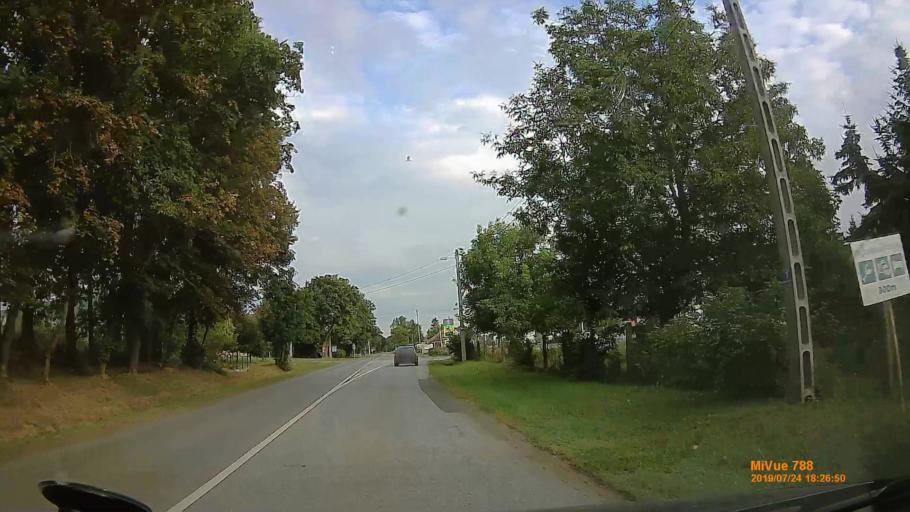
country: HU
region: Borsod-Abauj-Zemplen
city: Tarcal
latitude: 48.1416
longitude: 21.3356
